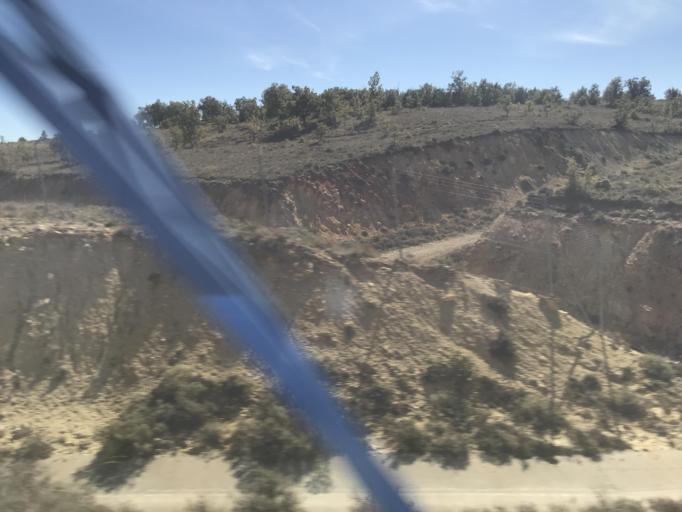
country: ES
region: Castille-La Mancha
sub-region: Provincia de Guadalajara
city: Anguita
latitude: 41.0913
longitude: -2.3970
